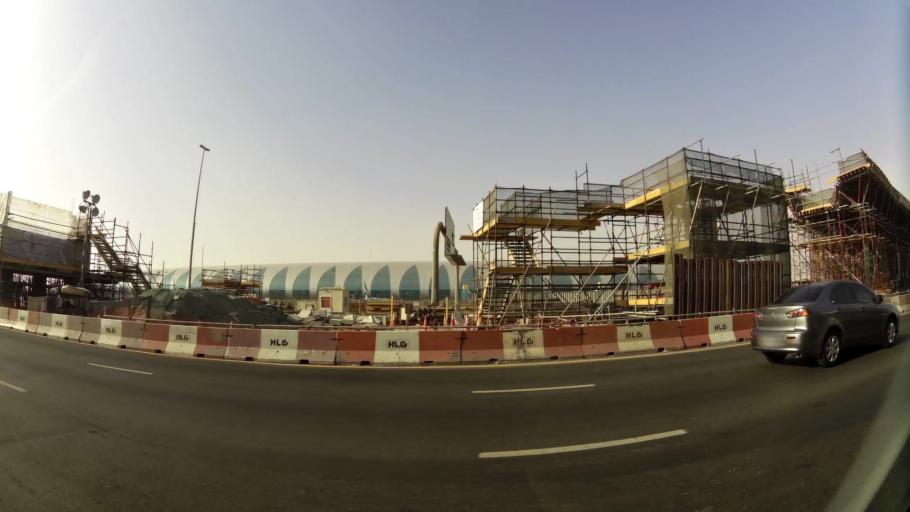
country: AE
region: Ash Shariqah
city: Sharjah
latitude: 25.2395
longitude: 55.3719
